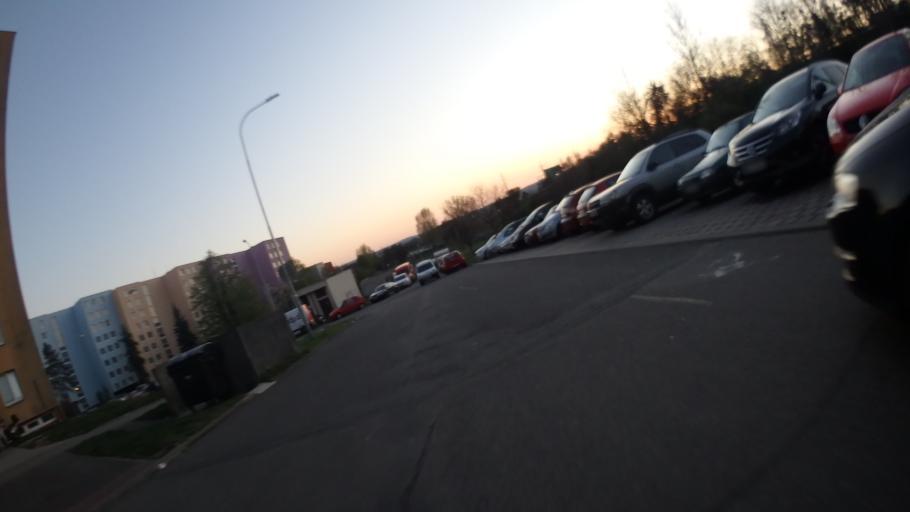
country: CZ
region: South Moravian
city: Ostopovice
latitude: 49.1707
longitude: 16.5583
